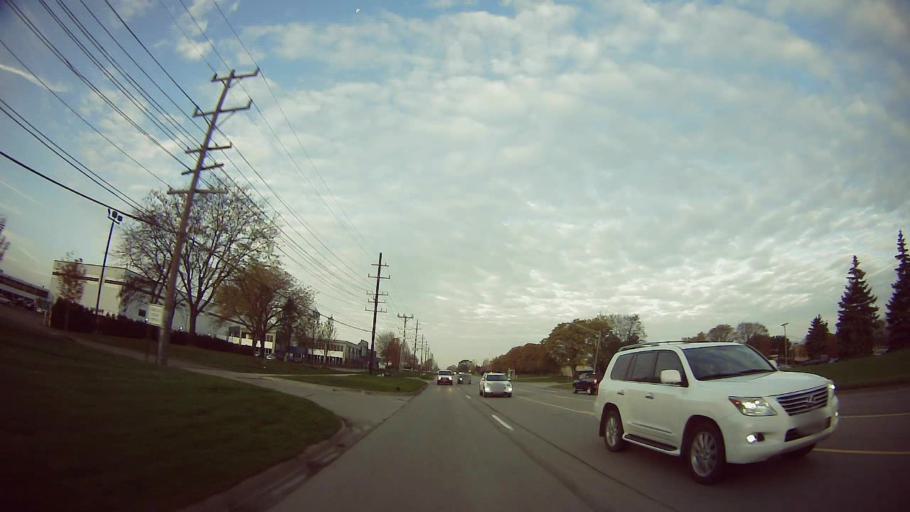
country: US
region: Michigan
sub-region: Macomb County
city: Sterling Heights
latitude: 42.5509
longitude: -83.0391
